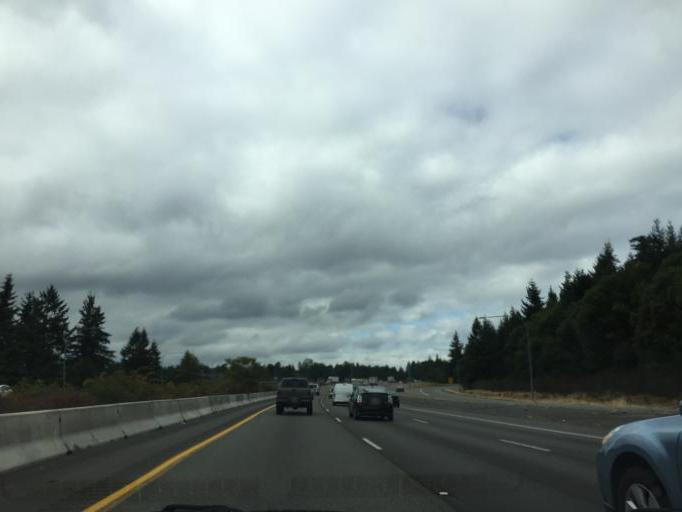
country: US
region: Washington
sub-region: Pierce County
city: Fort Lewis
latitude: 47.1064
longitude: -122.5826
